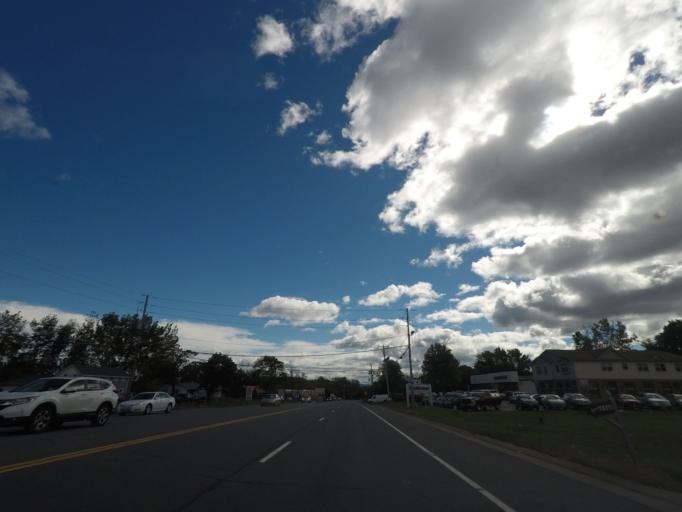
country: US
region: New York
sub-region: Saratoga County
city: Country Knolls
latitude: 42.8590
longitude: -73.7636
